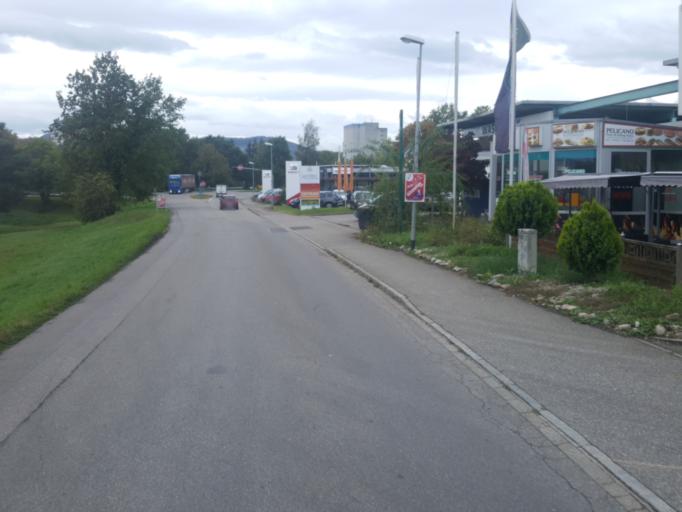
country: CH
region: Aargau
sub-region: Bezirk Rheinfelden
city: Kaiseraugst
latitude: 47.5473
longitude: 7.7386
